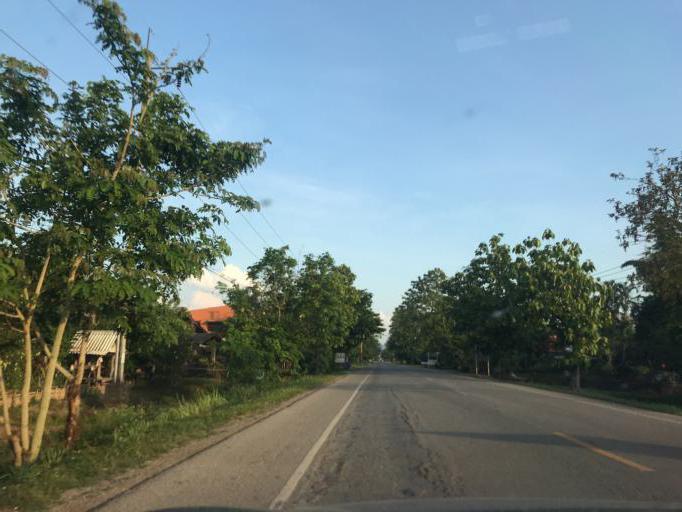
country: TH
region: Phayao
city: Chiang Kham
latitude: 19.5334
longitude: 100.2918
